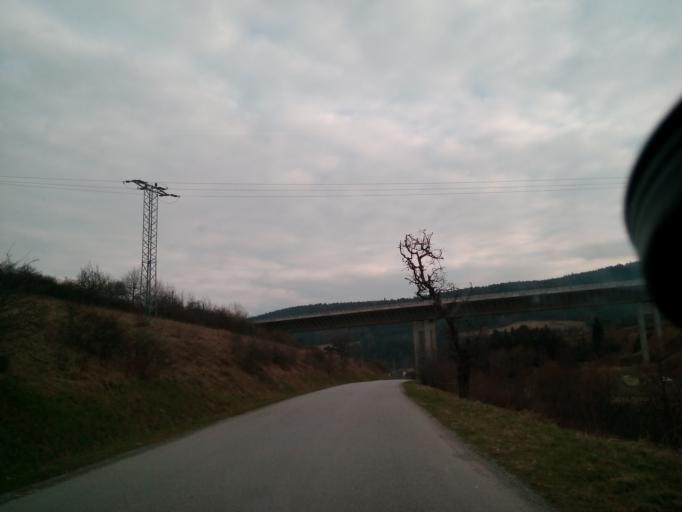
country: SK
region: Presovsky
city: Sabinov
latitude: 49.0286
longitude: 21.0197
